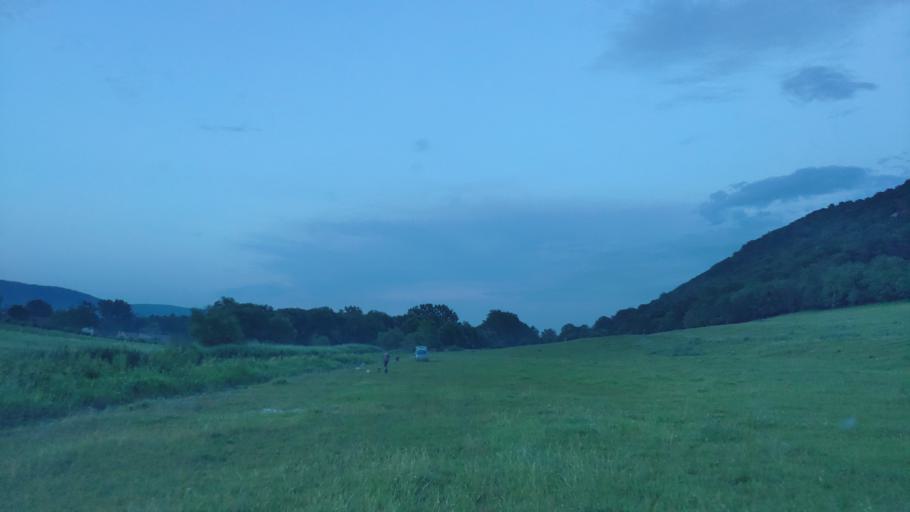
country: SK
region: Kosicky
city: Medzev
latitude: 48.5837
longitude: 20.8062
